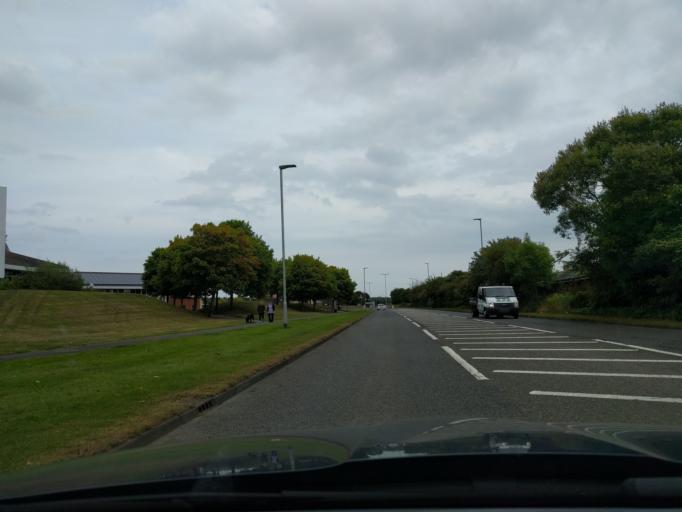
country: GB
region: England
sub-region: Northumberland
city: Ashington
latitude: 55.1842
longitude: -1.5836
